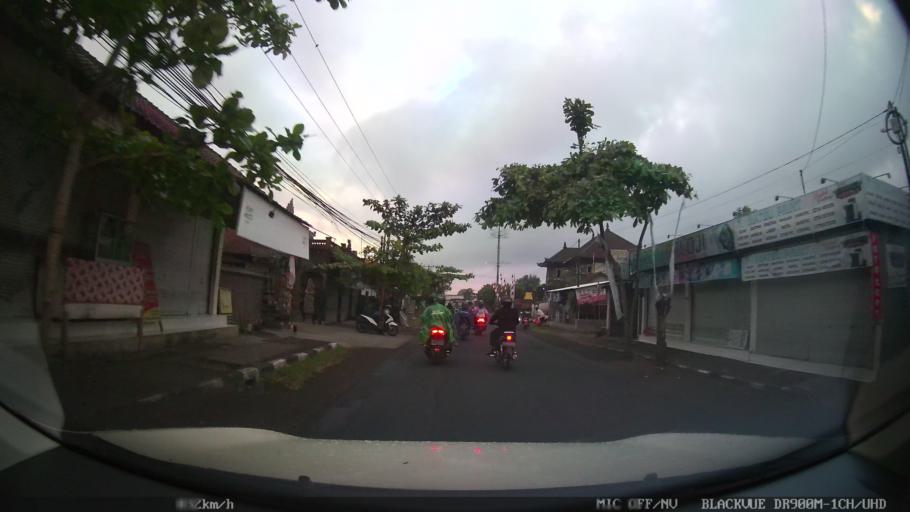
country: ID
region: Bali
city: Banjar Parekan
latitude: -8.5649
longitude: 115.2204
